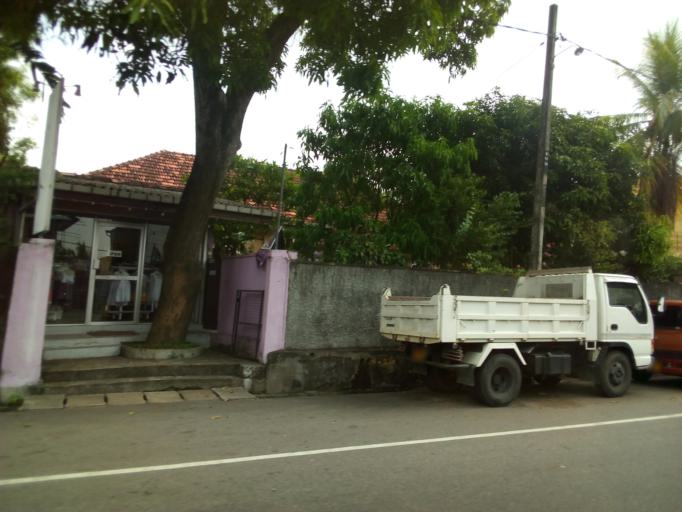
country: LK
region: Western
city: Maharagama
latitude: 6.8593
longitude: 79.9069
